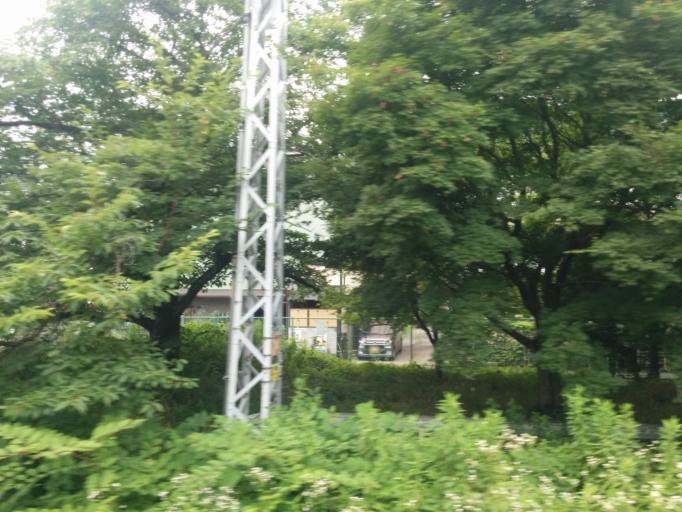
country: JP
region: Kyoto
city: Muko
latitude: 35.0093
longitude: 135.6831
